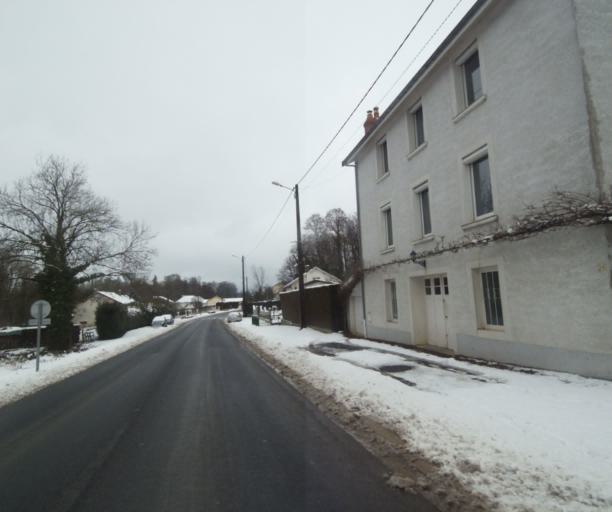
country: FR
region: Champagne-Ardenne
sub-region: Departement de la Haute-Marne
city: Wassy
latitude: 48.4748
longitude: 4.9706
